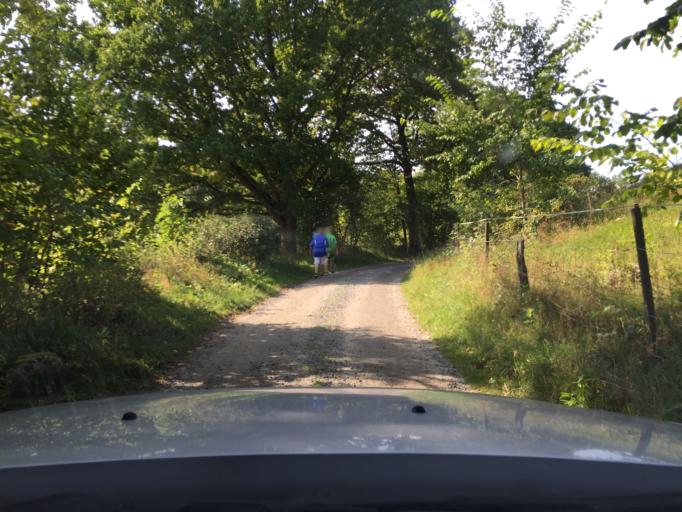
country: SE
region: Skane
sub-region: Kristianstads Kommun
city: Degeberga
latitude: 55.7275
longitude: 14.1218
